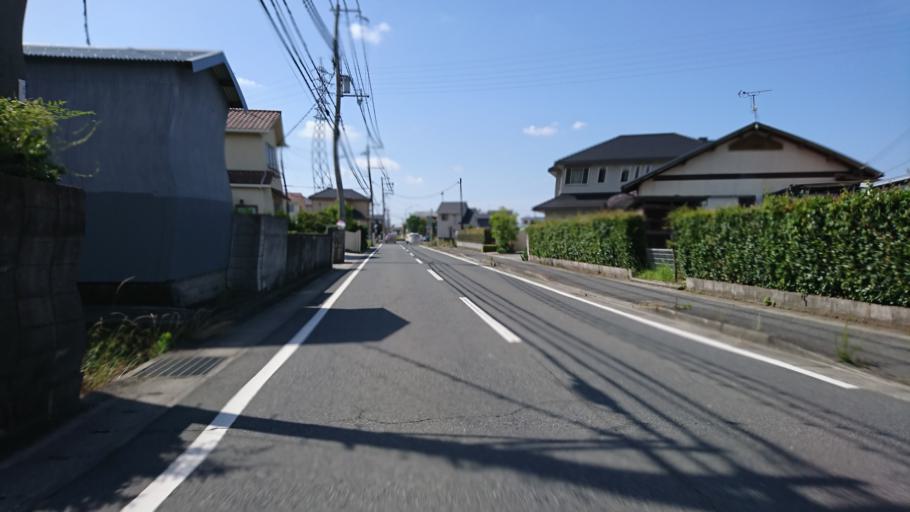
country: JP
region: Hyogo
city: Shirahamacho-usazakiminami
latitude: 34.7906
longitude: 134.7504
